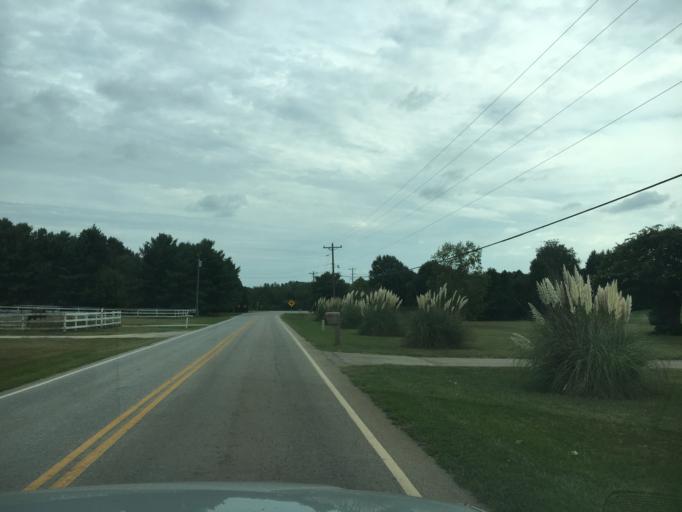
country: US
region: South Carolina
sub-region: Spartanburg County
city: Duncan
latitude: 34.9088
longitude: -82.1634
